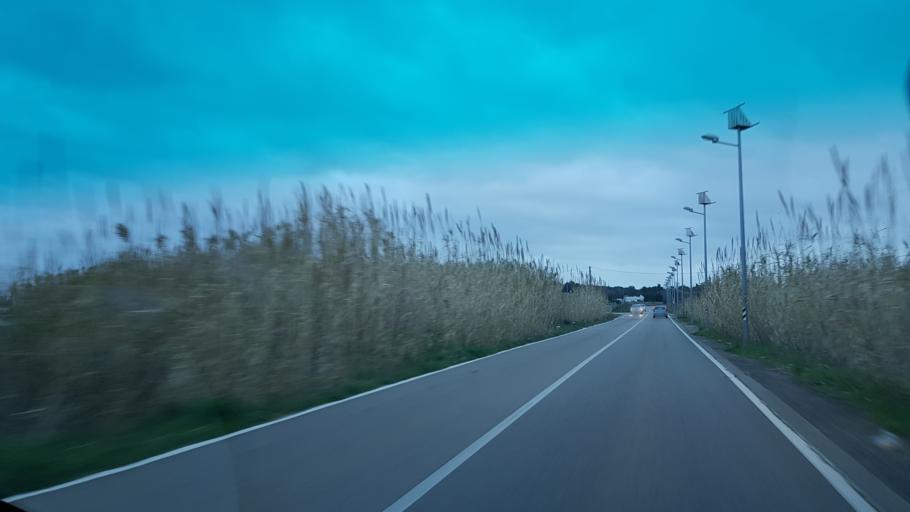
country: IT
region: Apulia
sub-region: Provincia di Brindisi
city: Torchiarolo
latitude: 40.5288
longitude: 18.0695
